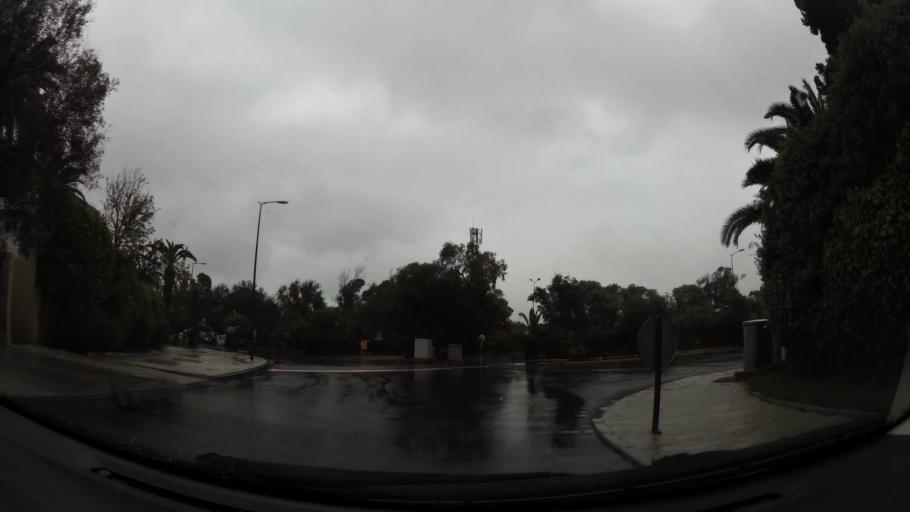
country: MA
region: Grand Casablanca
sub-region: Casablanca
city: Casablanca
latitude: 33.5889
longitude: -7.6603
